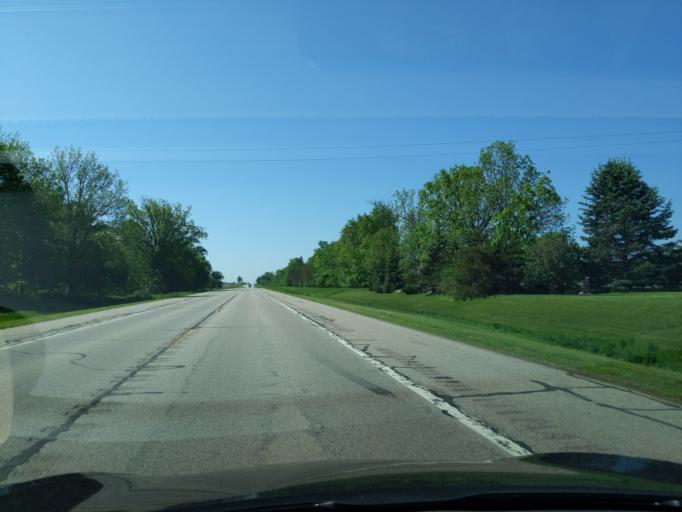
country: US
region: Michigan
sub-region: Ingham County
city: Webberville
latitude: 42.5805
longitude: -84.1928
